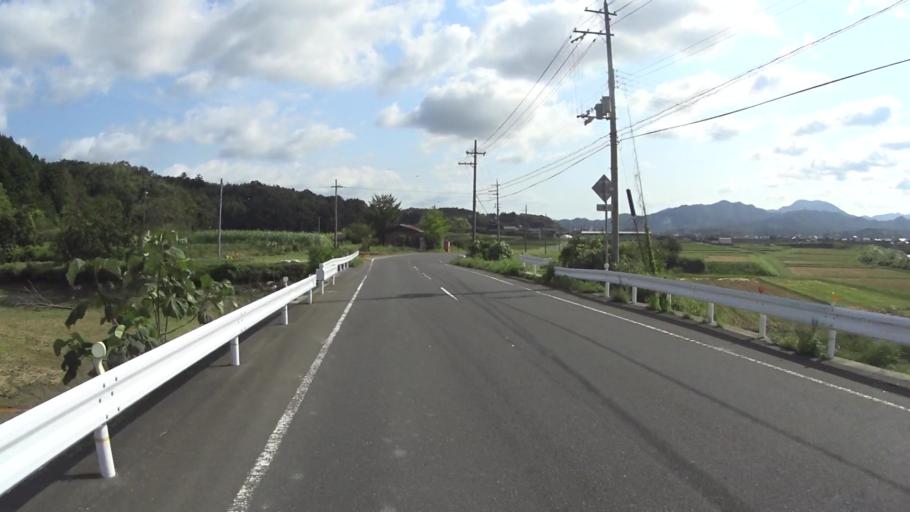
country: JP
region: Kyoto
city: Miyazu
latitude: 35.6251
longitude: 135.0834
